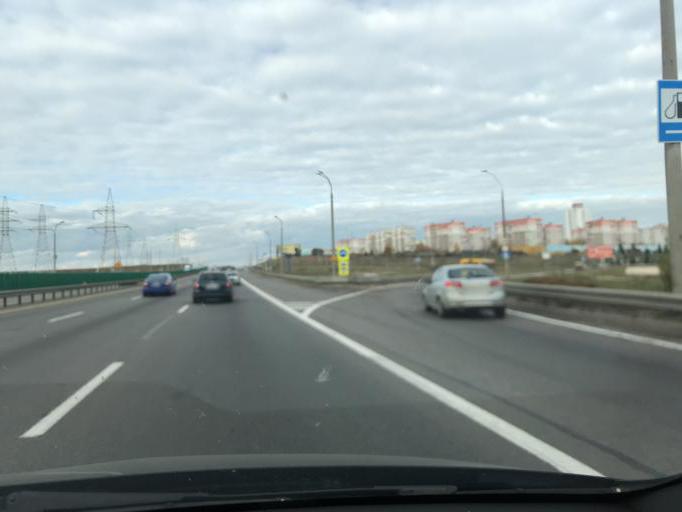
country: BY
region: Minsk
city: Malinovka
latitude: 53.8763
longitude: 27.4194
